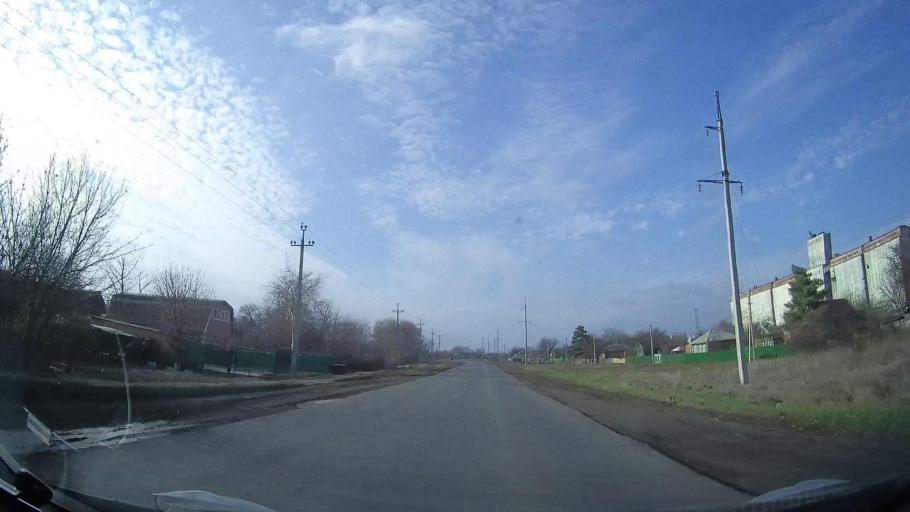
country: RU
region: Rostov
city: Mechetinskaya
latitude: 46.7863
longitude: 40.4789
